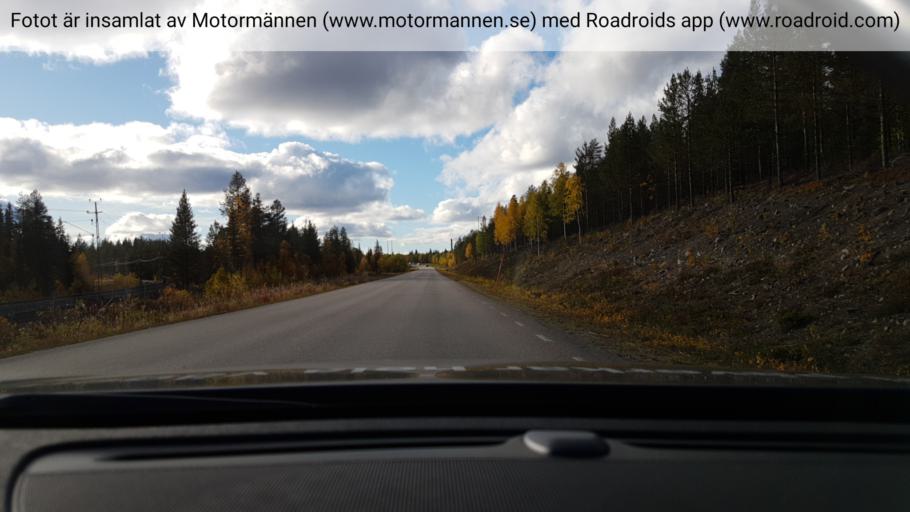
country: SE
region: Norrbotten
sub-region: Gallivare Kommun
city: Malmberget
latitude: 67.1606
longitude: 20.6749
